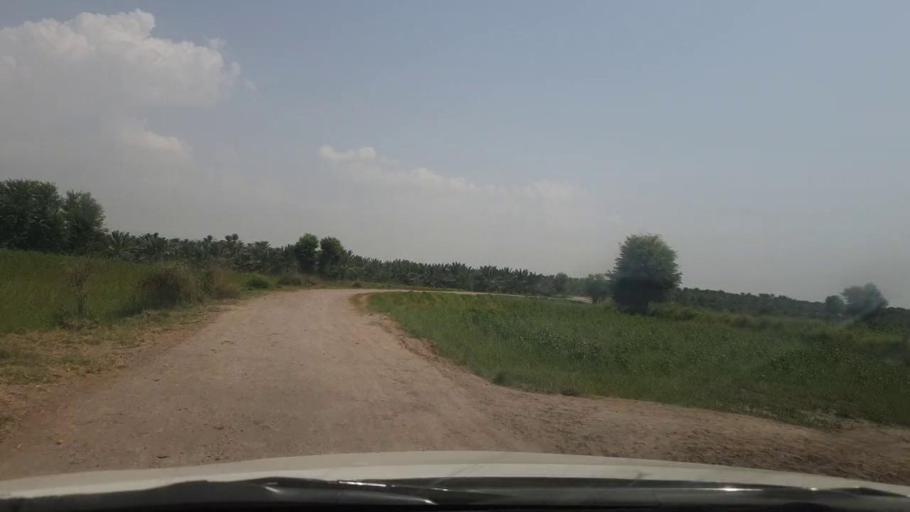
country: PK
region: Sindh
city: Khairpur
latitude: 27.5574
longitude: 68.8388
